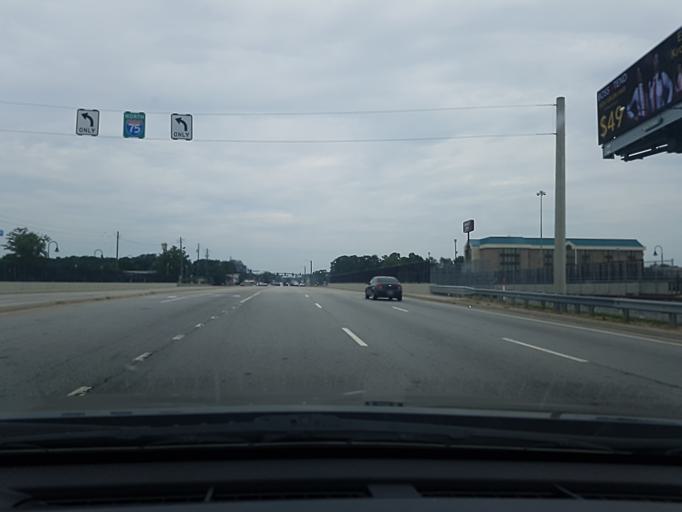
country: US
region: Georgia
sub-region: Clayton County
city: Morrow
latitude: 33.5758
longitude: -84.3414
